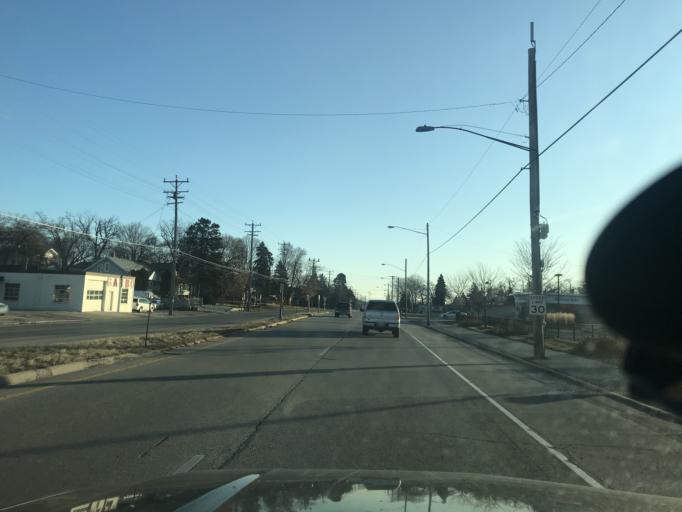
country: US
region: Wisconsin
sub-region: Kenosha County
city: Kenosha
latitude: 42.5662
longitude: -87.8641
